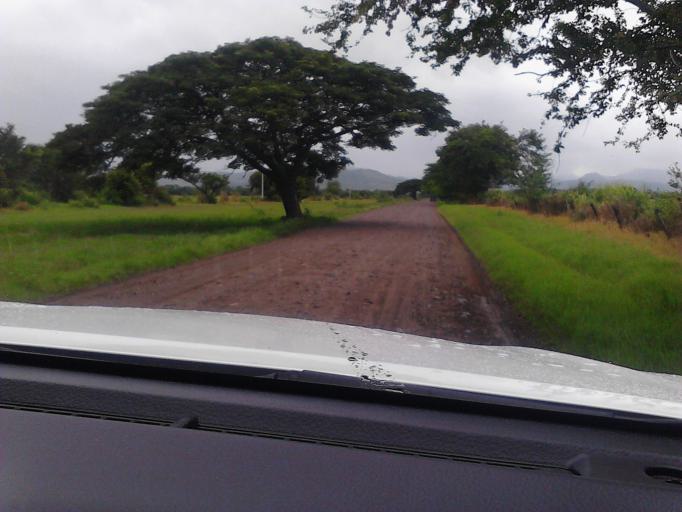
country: NI
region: Matagalpa
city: Ciudad Dario
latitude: 12.8947
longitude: -86.1520
